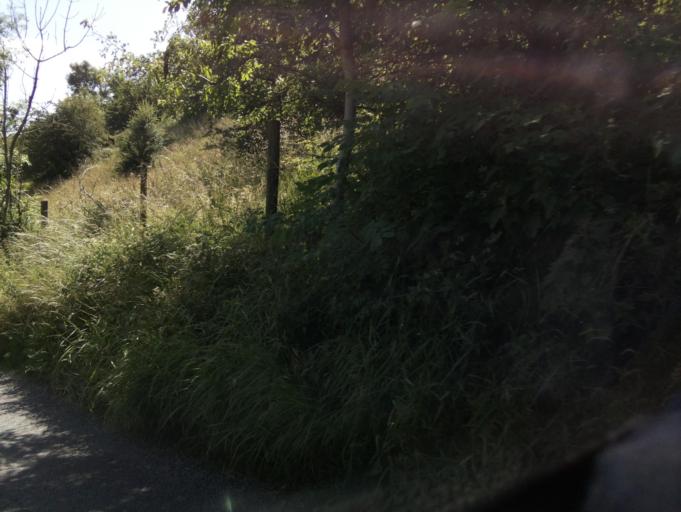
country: GB
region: England
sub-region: Derbyshire
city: Buxton
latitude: 53.1808
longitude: -1.8604
